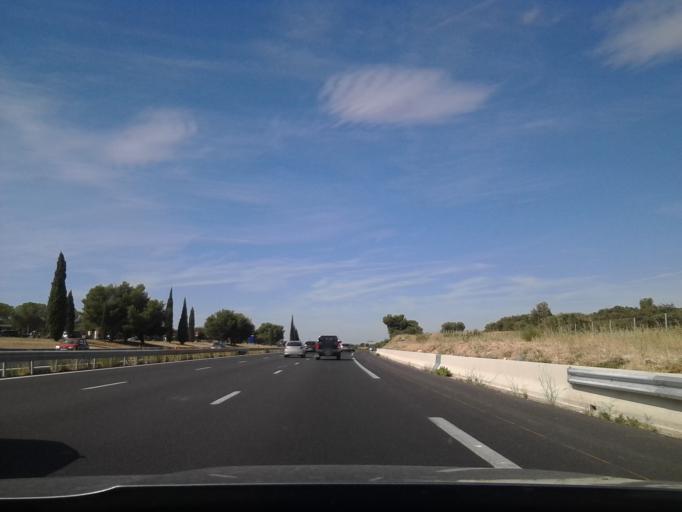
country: FR
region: Languedoc-Roussillon
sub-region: Departement de l'Herault
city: Loupian
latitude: 43.4649
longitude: 3.6322
